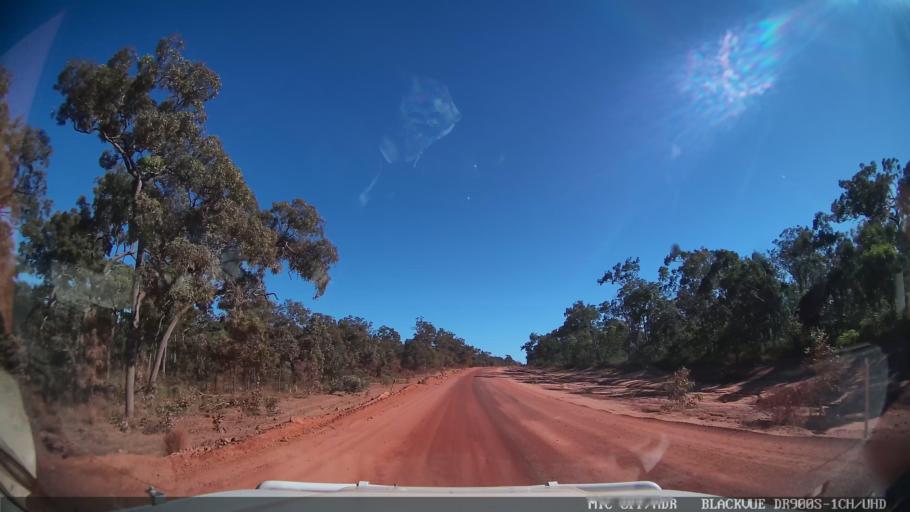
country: AU
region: Queensland
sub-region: Torres
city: Thursday Island
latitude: -11.4005
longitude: 142.3580
